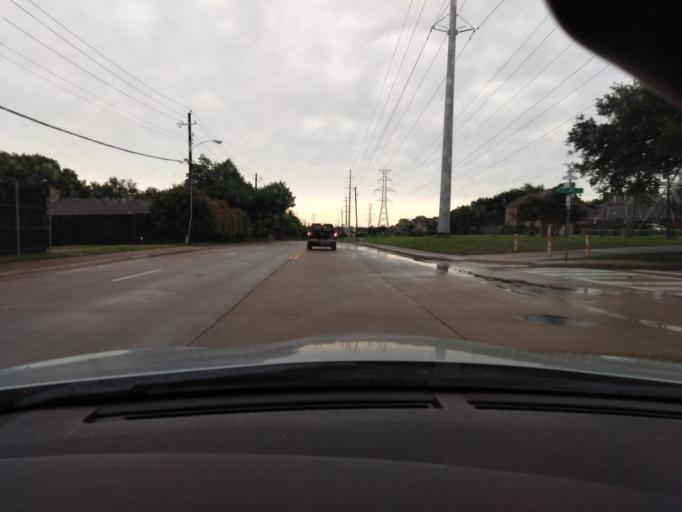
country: US
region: Texas
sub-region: Dallas County
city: Addison
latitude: 32.9844
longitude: -96.7786
